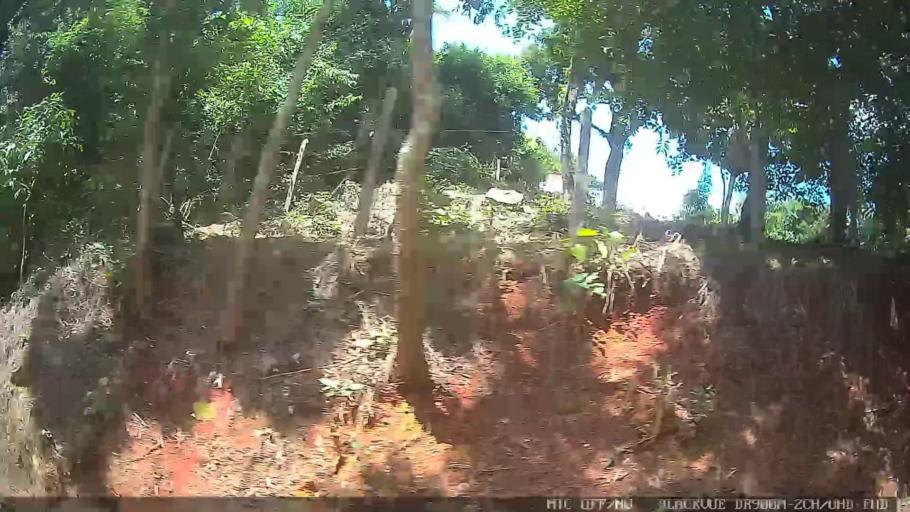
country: BR
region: Minas Gerais
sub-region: Extrema
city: Extrema
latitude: -22.8706
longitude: -46.3300
